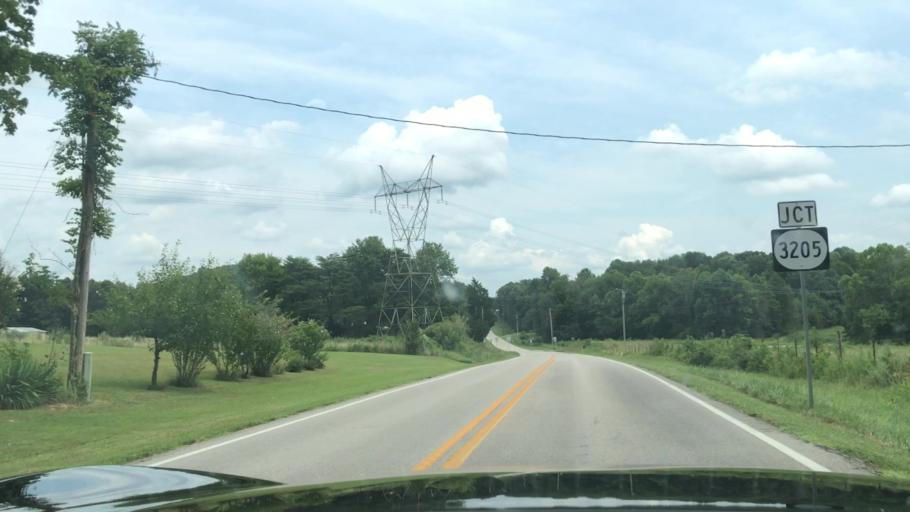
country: US
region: Kentucky
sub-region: Butler County
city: Morgantown
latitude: 37.1720
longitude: -86.8220
